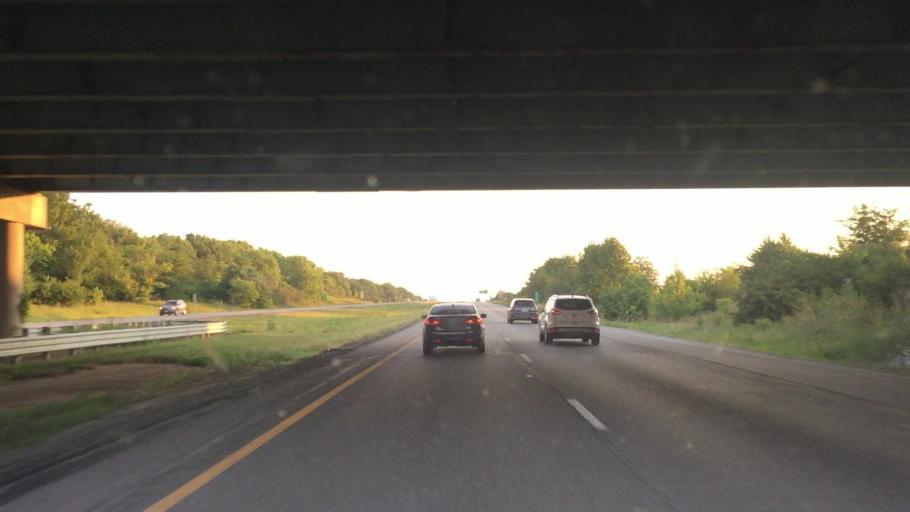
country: US
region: Missouri
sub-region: Clay County
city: Pleasant Valley
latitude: 39.2887
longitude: -94.5101
